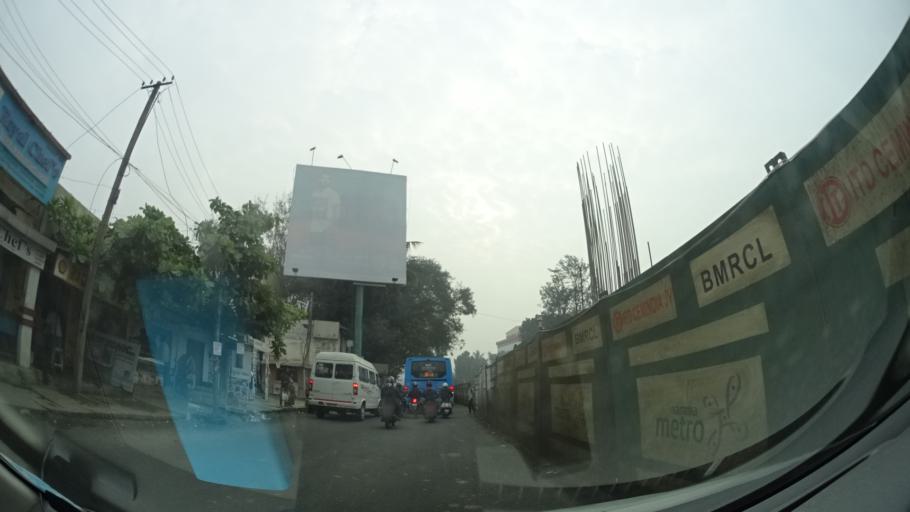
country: IN
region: Karnataka
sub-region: Bangalore Urban
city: Bangalore
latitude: 12.9975
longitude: 77.6905
